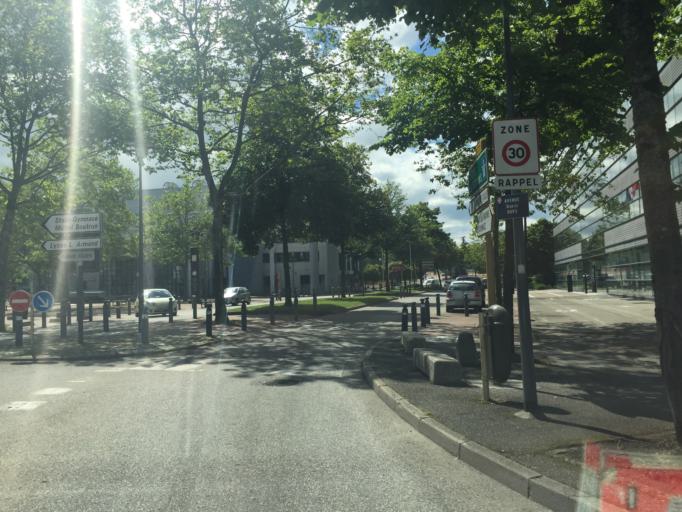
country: FR
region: Rhone-Alpes
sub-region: Departement de la Savoie
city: Bassens
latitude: 45.5931
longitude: 5.9185
